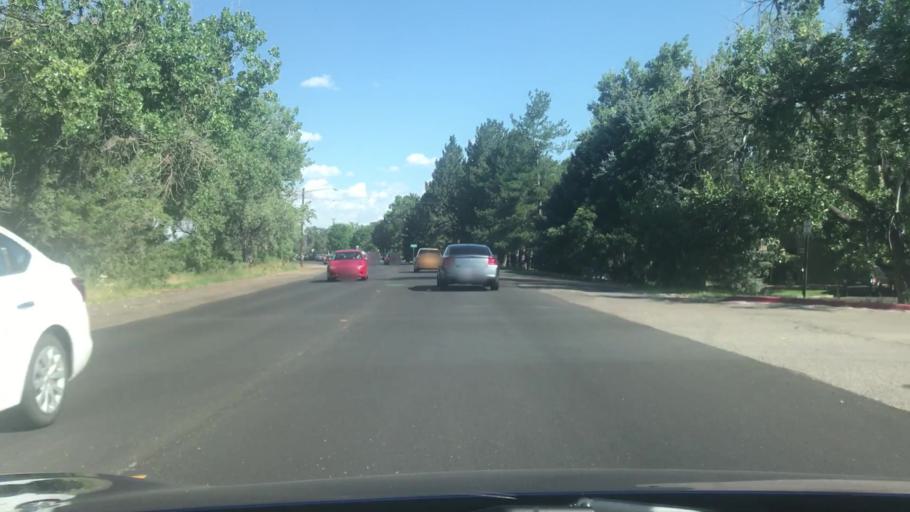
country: US
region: Colorado
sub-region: Arapahoe County
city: Glendale
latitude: 39.6981
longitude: -104.9256
